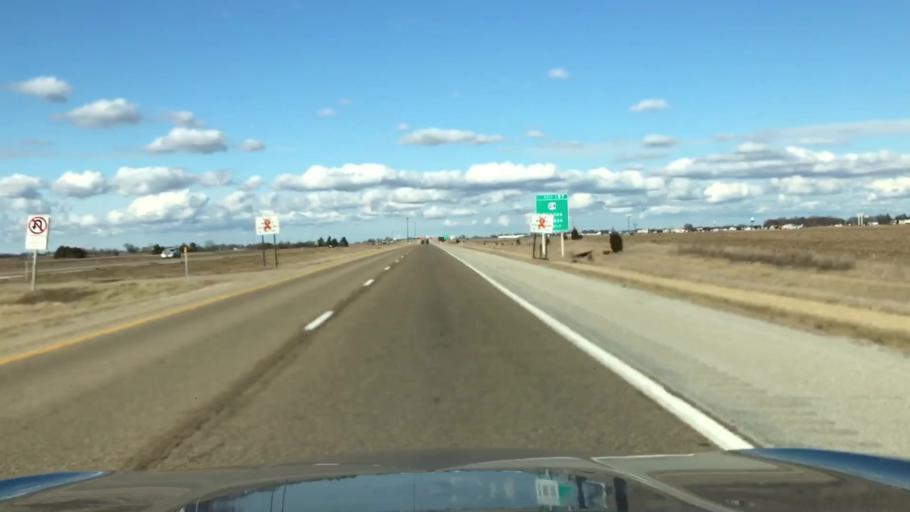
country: US
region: Illinois
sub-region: McLean County
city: Chenoa
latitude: 40.7287
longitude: -88.7371
